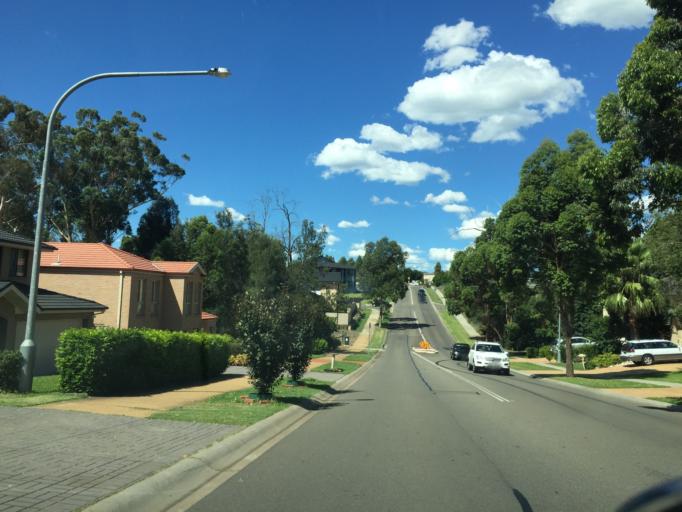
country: AU
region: New South Wales
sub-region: The Hills Shire
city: Glenhaven
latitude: -33.7102
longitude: 150.9714
